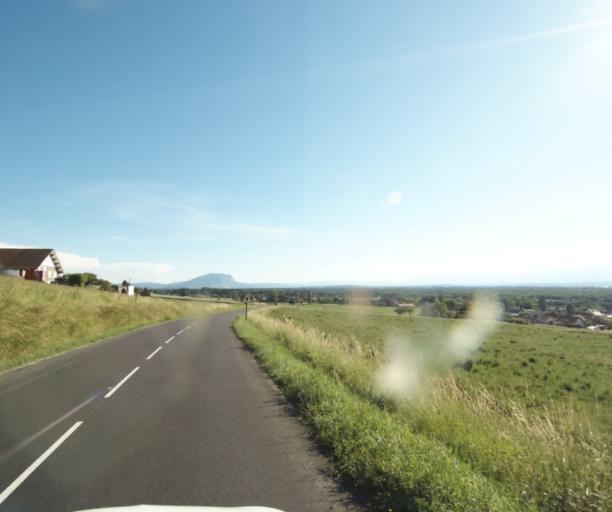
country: FR
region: Rhone-Alpes
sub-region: Departement de la Haute-Savoie
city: Loisin
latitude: 46.2916
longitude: 6.3166
